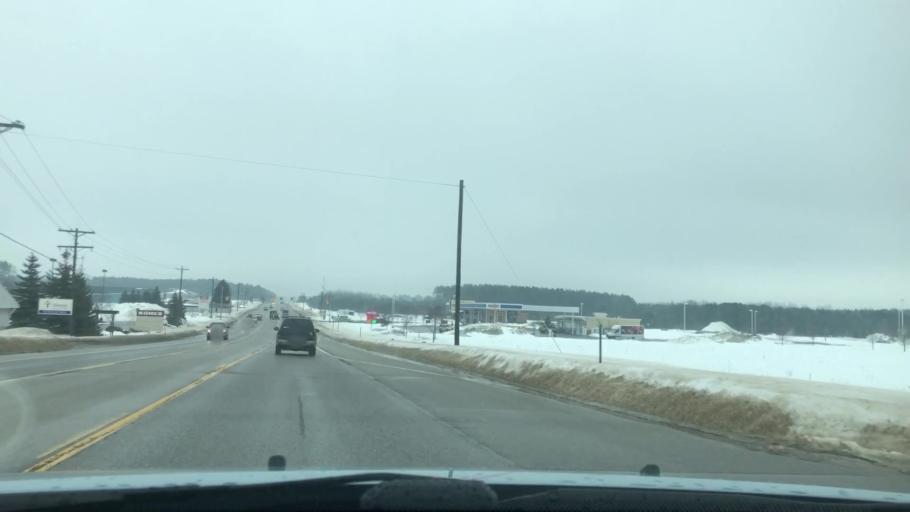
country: US
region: Michigan
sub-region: Otsego County
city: Gaylord
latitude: 45.0270
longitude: -84.7256
